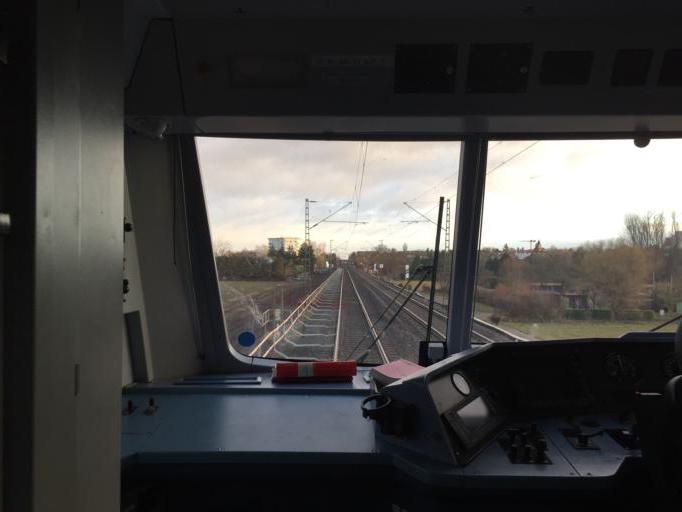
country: DE
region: Hesse
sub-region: Regierungsbezirk Darmstadt
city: Frankfurt am Main
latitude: 50.1494
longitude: 8.6478
